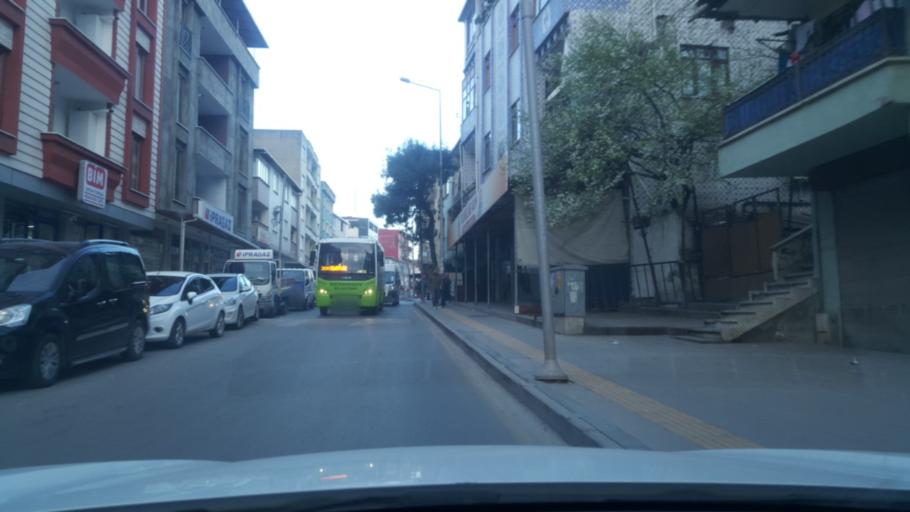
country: TR
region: Kocaeli
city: Tavsancil
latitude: 40.7852
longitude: 29.5456
